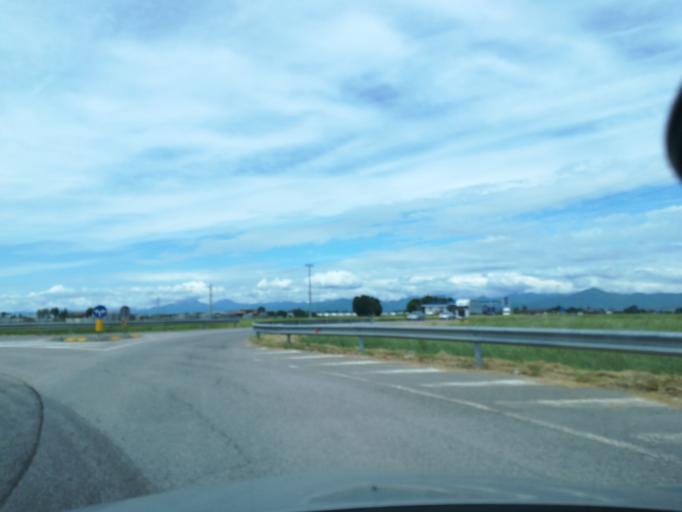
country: IT
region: Lombardy
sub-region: Provincia di Bergamo
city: Cividate al Piano
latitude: 45.5555
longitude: 9.8228
